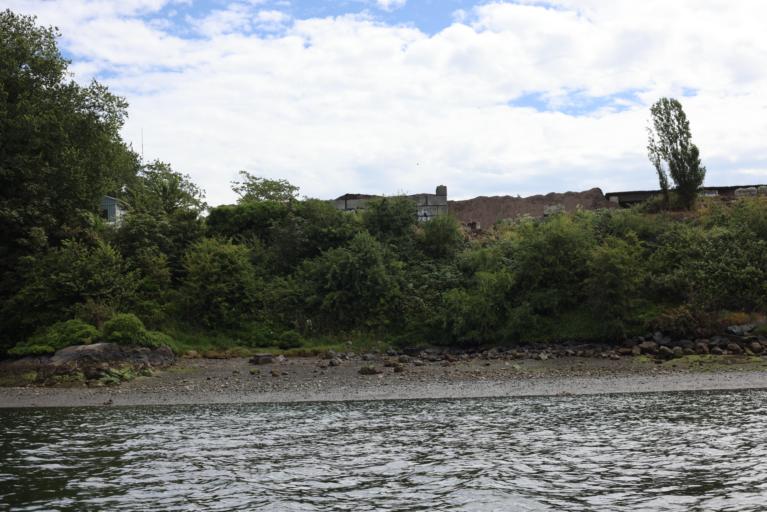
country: CA
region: British Columbia
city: Victoria
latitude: 48.4351
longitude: -123.3784
